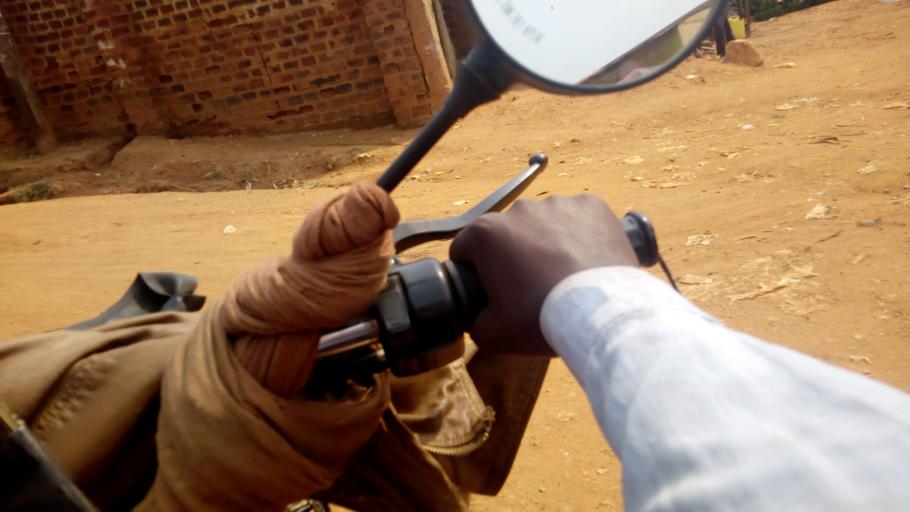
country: UG
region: Central Region
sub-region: Wakiso District
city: Kireka
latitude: 0.3249
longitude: 32.6537
